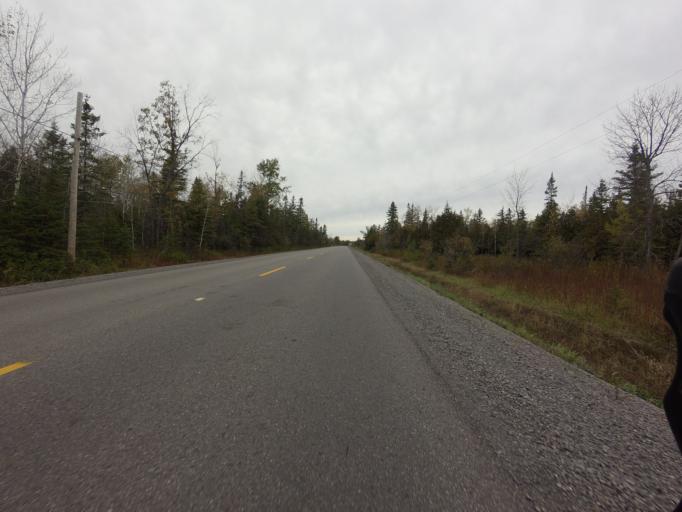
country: CA
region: Ontario
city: Brockville
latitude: 44.7927
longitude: -75.7817
